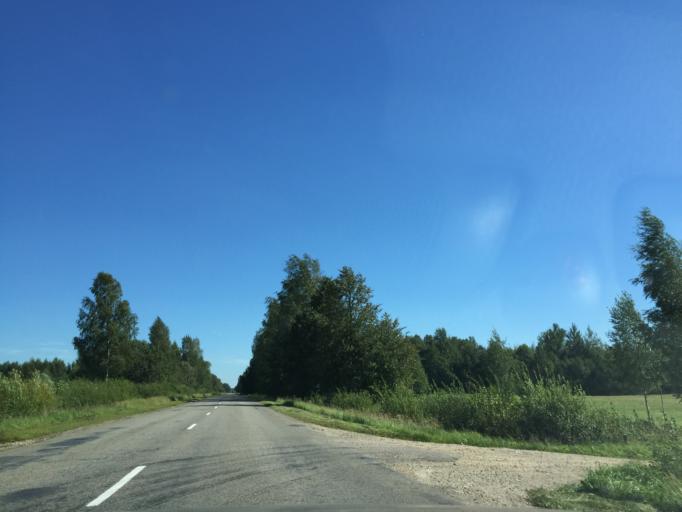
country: LV
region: Akniste
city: Akniste
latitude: 56.1523
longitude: 25.7731
